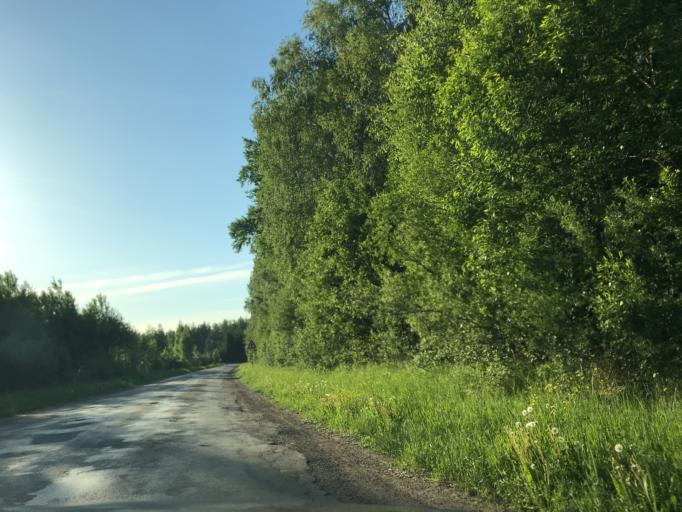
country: LV
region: Ozolnieku
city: Ozolnieki
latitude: 56.6033
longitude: 23.7945
